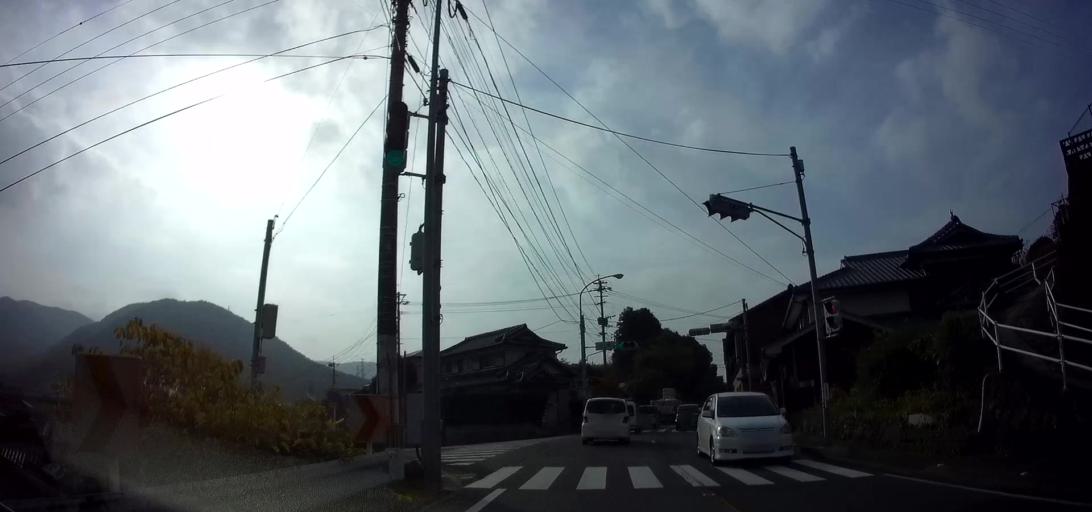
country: JP
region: Nagasaki
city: Shimabara
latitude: 32.7663
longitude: 130.2142
